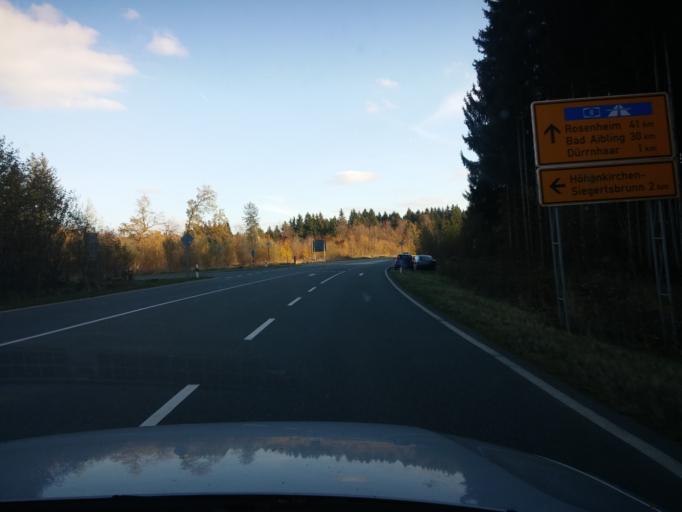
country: DE
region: Bavaria
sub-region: Upper Bavaria
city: Hohenkirchen-Siegertsbrunn
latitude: 48.0089
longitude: 11.7213
